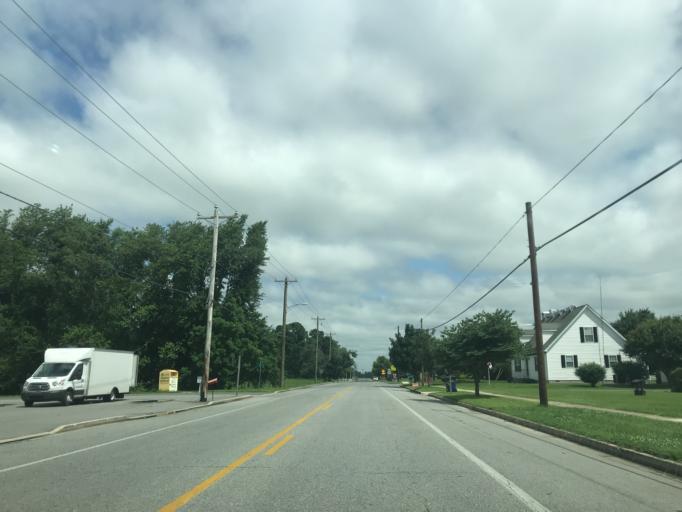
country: US
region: Maryland
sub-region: Caroline County
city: Ridgely
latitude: 38.9493
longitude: -75.8849
